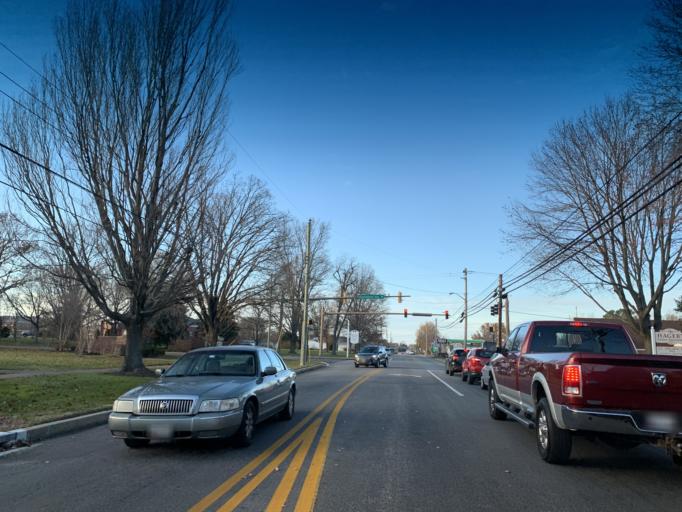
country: US
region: Maryland
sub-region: Kent County
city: Chestertown
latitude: 39.2192
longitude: -76.0673
